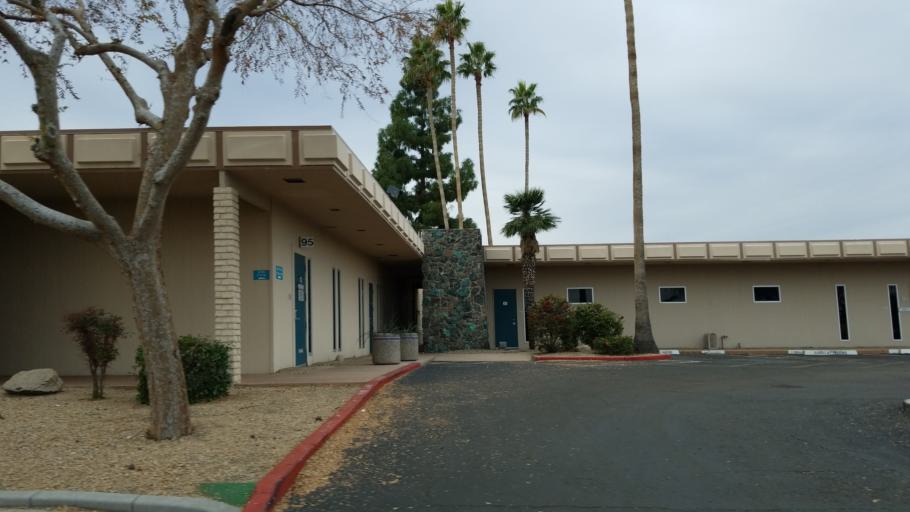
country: US
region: Arizona
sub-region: Maricopa County
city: Sun City
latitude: 33.6017
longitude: -112.2814
